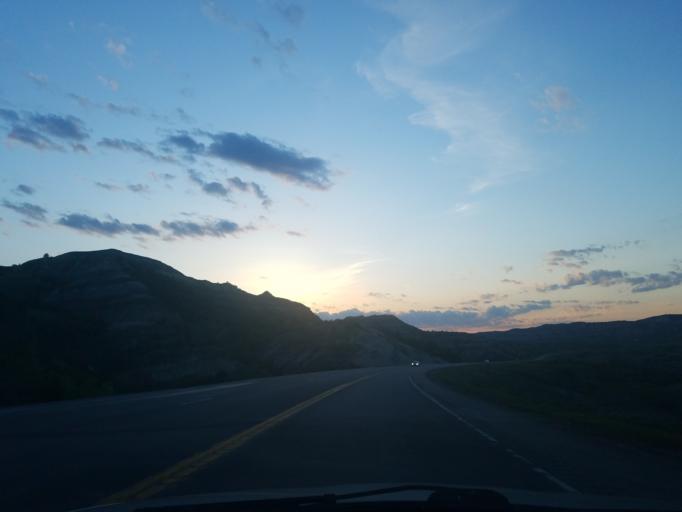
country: US
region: North Dakota
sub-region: McKenzie County
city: Watford City
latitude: 47.5736
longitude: -103.2434
